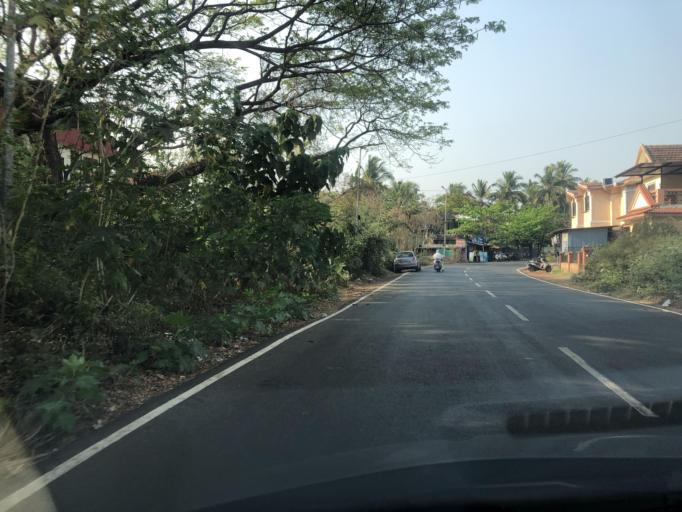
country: IN
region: Goa
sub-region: North Goa
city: Serula
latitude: 15.5289
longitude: 73.8290
